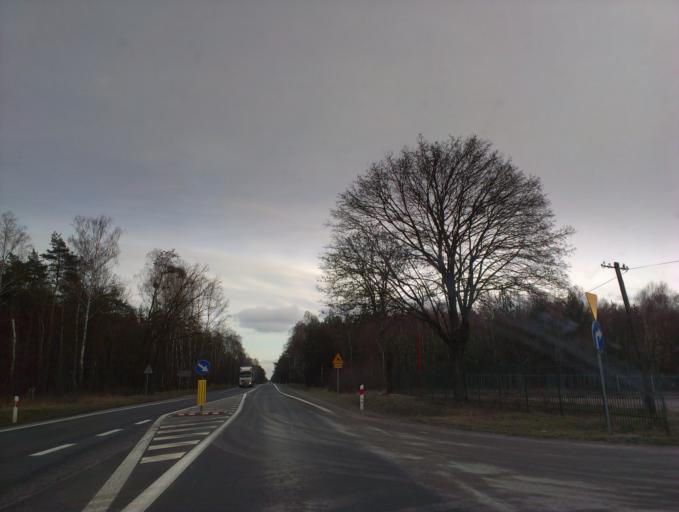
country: PL
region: Masovian Voivodeship
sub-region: Powiat sierpecki
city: Szczutowo
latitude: 52.8819
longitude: 19.5911
